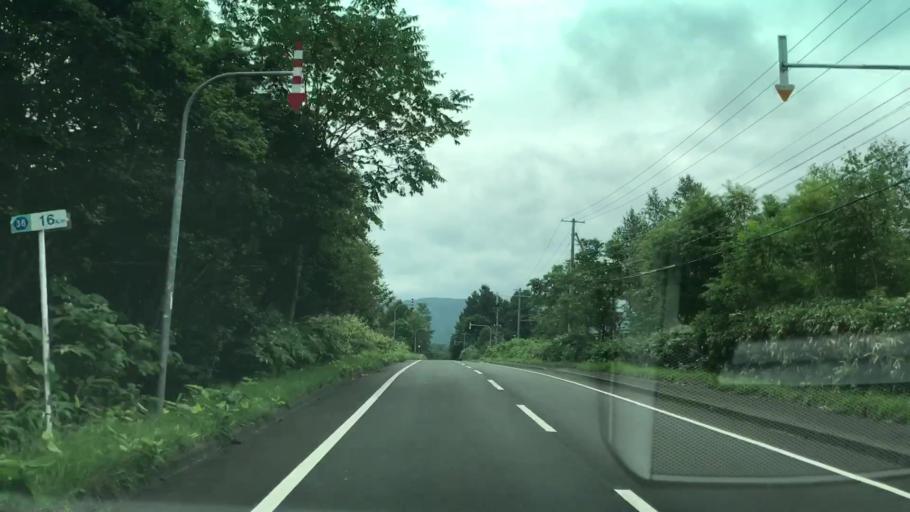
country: JP
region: Hokkaido
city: Yoichi
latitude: 43.0685
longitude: 140.8190
